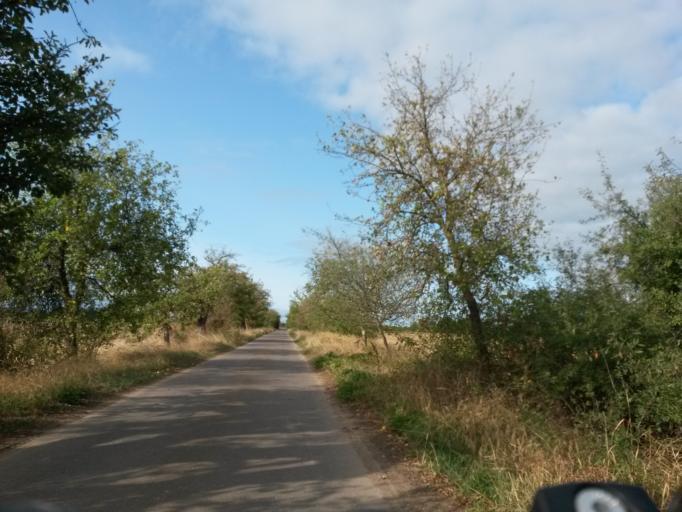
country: DE
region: Saxony-Anhalt
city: Jerichow
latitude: 52.4915
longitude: 11.9742
